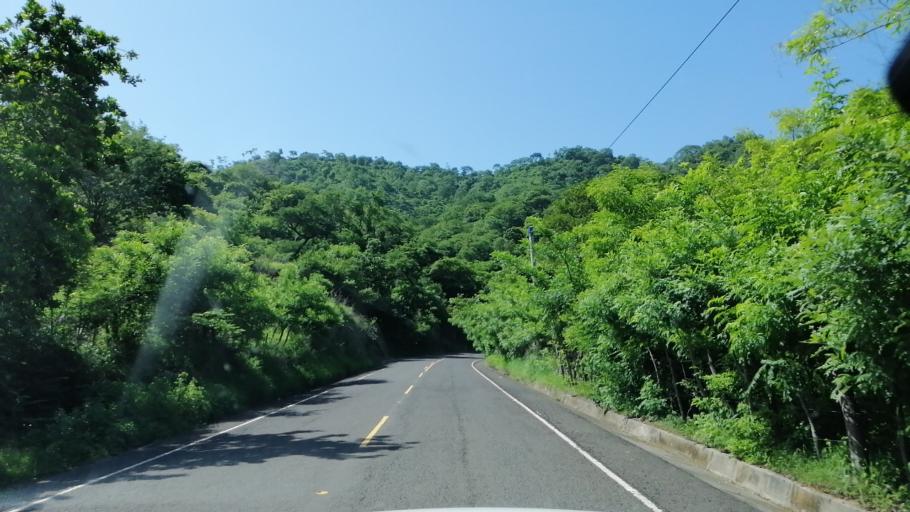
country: HN
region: Lempira
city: La Virtud
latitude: 13.9808
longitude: -88.7572
